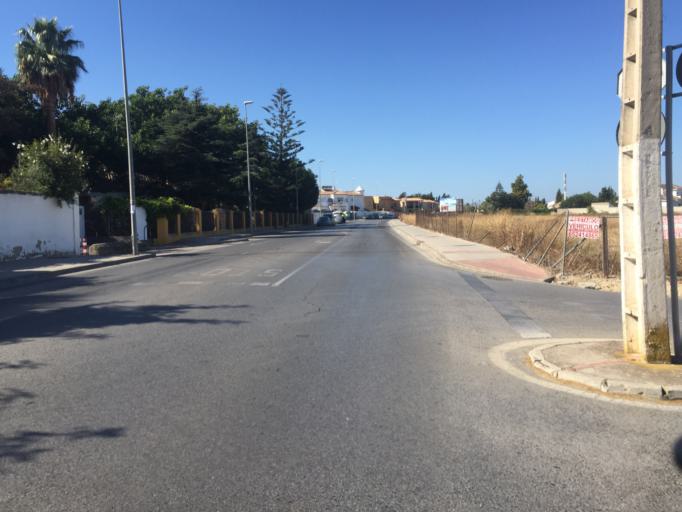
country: ES
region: Andalusia
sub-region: Provincia de Cadiz
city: Chiclana de la Frontera
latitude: 36.4158
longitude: -6.1597
